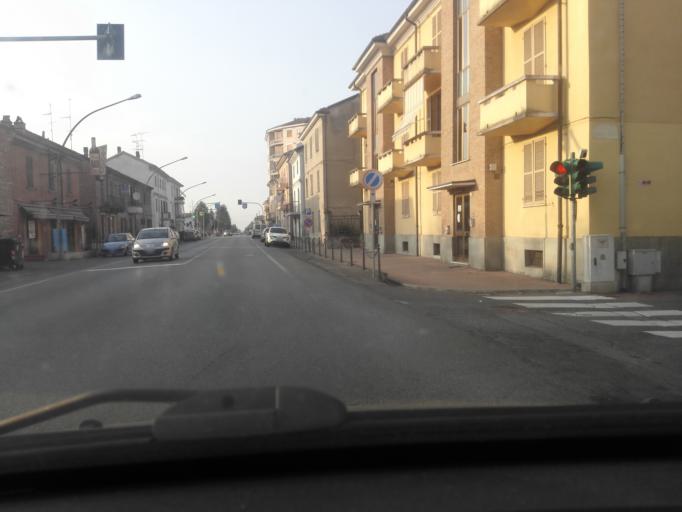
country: IT
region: Piedmont
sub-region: Provincia di Alessandria
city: Villalvernia
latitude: 44.8163
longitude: 8.8549
